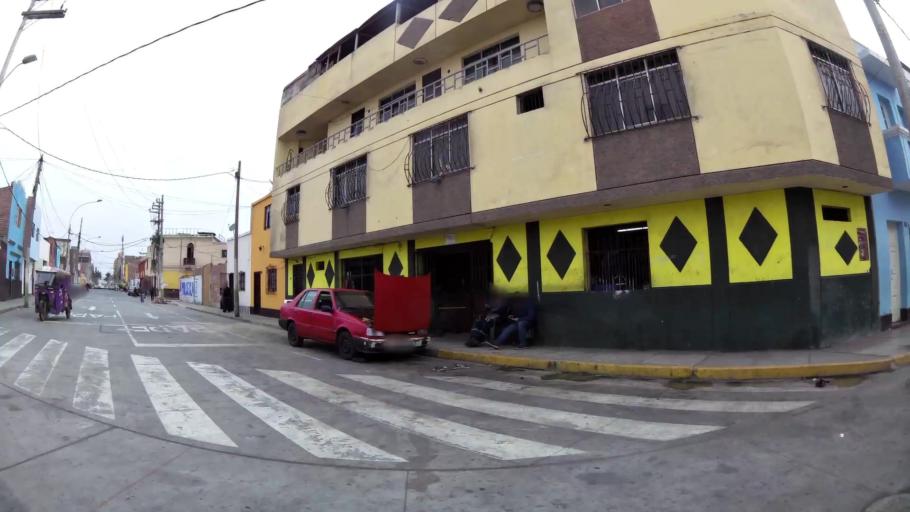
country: PE
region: Callao
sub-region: Callao
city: Callao
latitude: -12.0575
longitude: -77.1387
